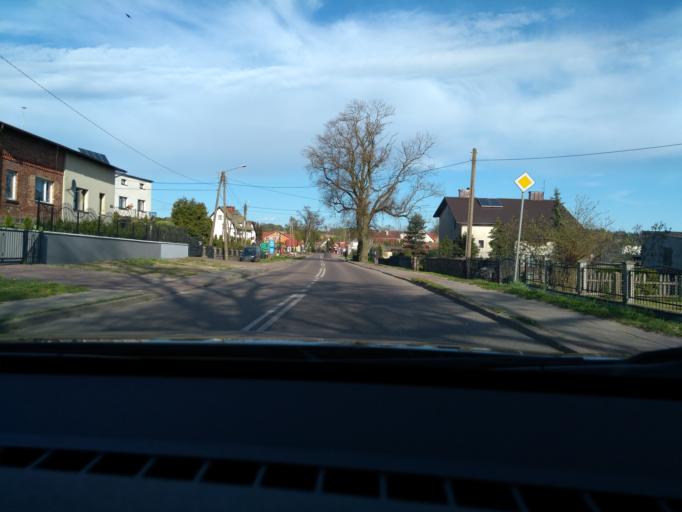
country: PL
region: Pomeranian Voivodeship
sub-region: Powiat kartuski
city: Suleczyno
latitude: 54.3257
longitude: 17.7918
